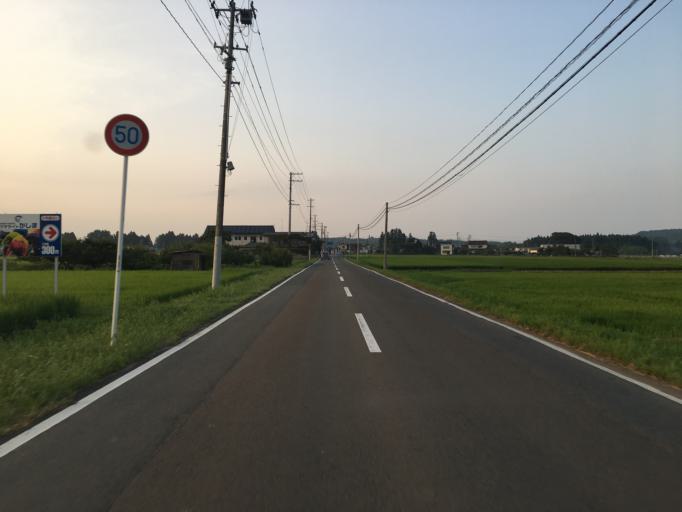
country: JP
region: Fukushima
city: Namie
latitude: 37.7166
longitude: 140.9287
